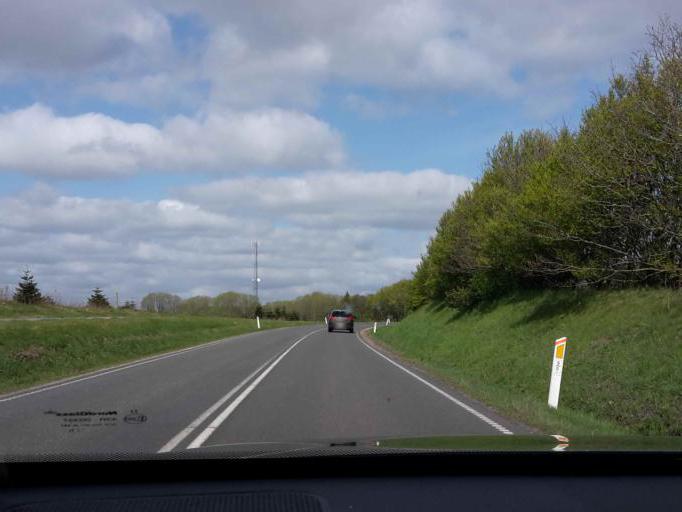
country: DK
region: South Denmark
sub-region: Varde Kommune
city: Olgod
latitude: 55.7287
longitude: 8.7185
